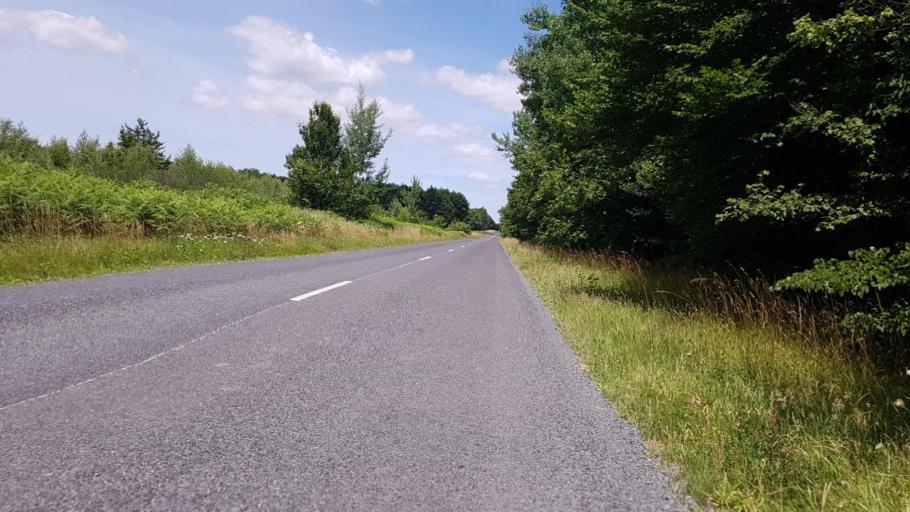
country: FR
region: Picardie
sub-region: Departement de l'Oise
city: Carlepont
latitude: 49.5235
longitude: 2.9836
